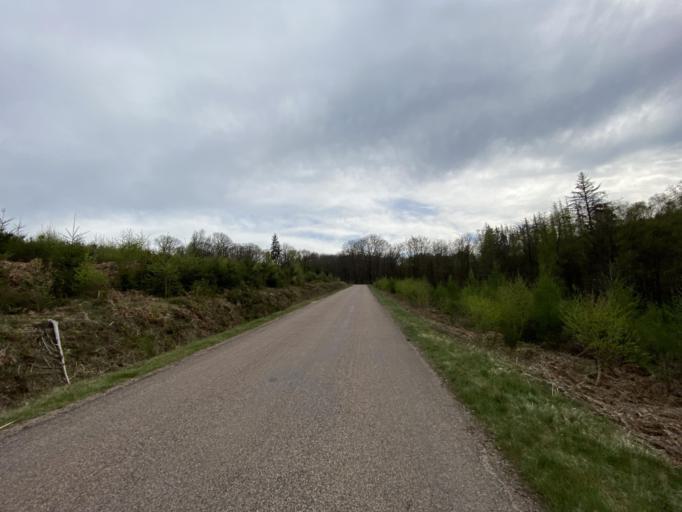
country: FR
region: Bourgogne
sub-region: Departement de la Cote-d'Or
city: Saulieu
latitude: 47.3083
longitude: 4.0878
